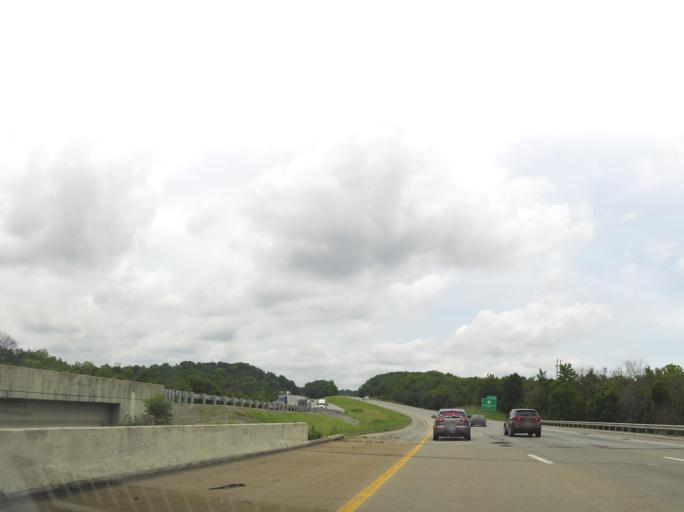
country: US
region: Kentucky
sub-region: Scott County
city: Georgetown
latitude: 38.3605
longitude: -84.5668
